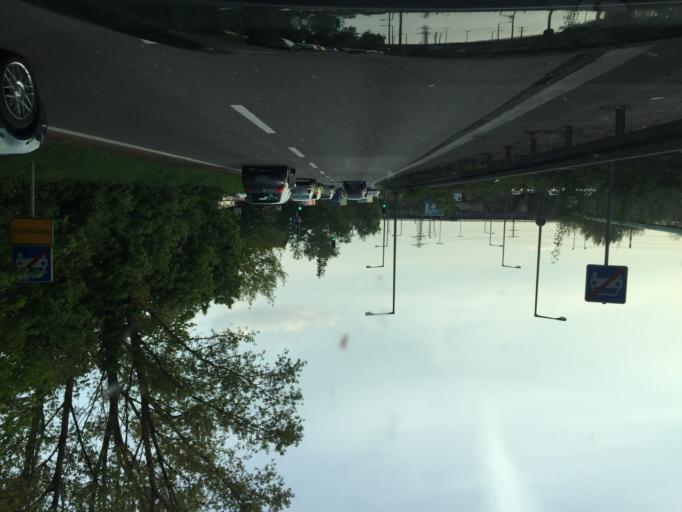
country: DE
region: Bavaria
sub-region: Regierungsbezirk Mittelfranken
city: Nuernberg
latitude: 49.4388
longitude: 11.0628
